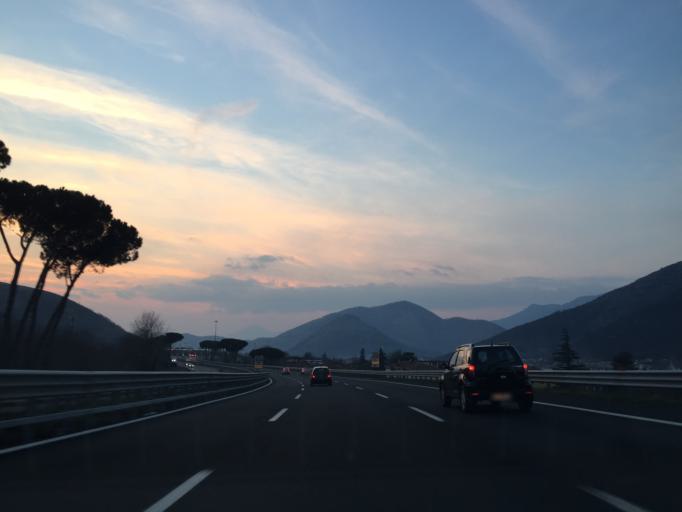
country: IT
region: Campania
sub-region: Provincia di Salerno
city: Piazza del Galdo-Sant'Angelo
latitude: 40.7721
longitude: 14.7349
